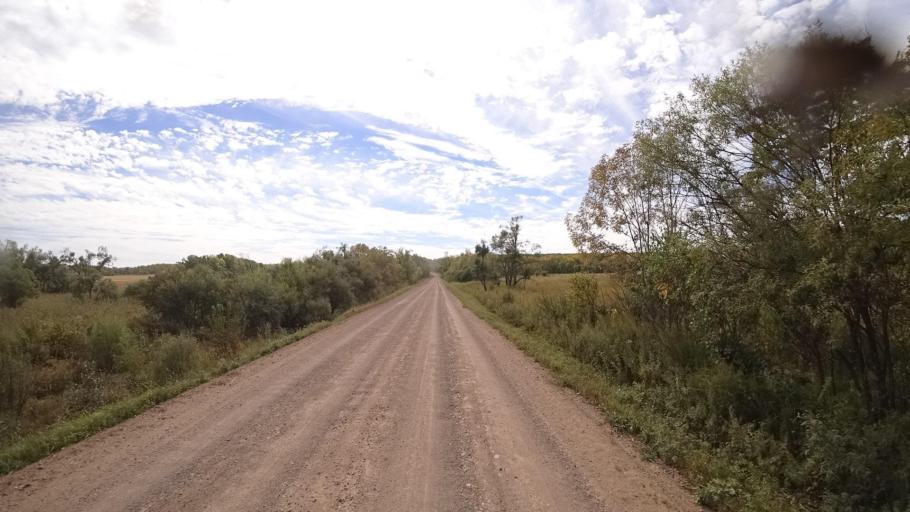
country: RU
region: Primorskiy
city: Yakovlevka
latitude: 44.5298
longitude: 133.5984
